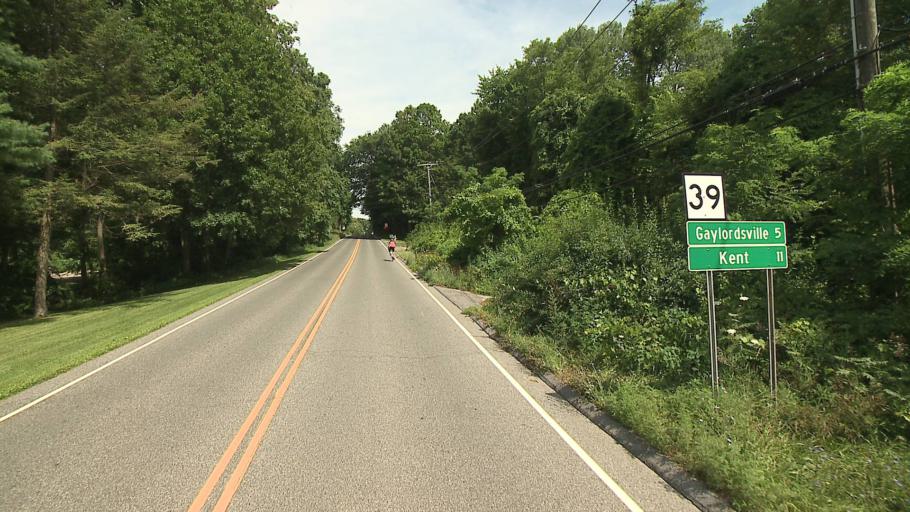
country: US
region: Connecticut
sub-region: Fairfield County
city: Sherman
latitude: 41.5804
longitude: -73.4972
